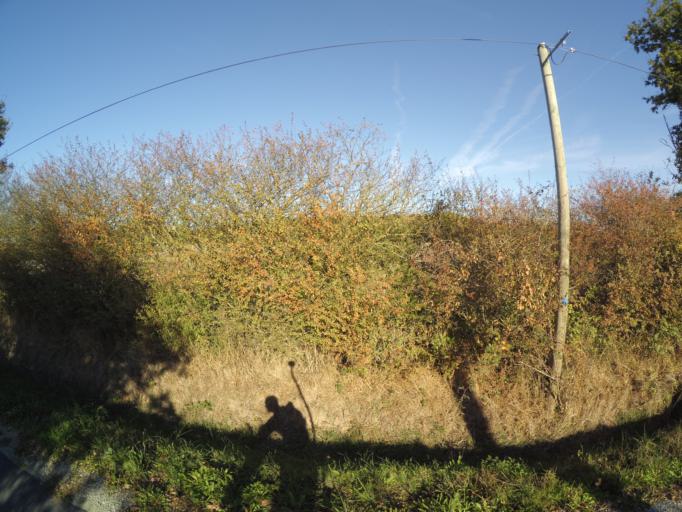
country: FR
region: Pays de la Loire
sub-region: Departement de la Loire-Atlantique
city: Saint-Lumine-de-Clisson
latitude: 47.0821
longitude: -1.3277
